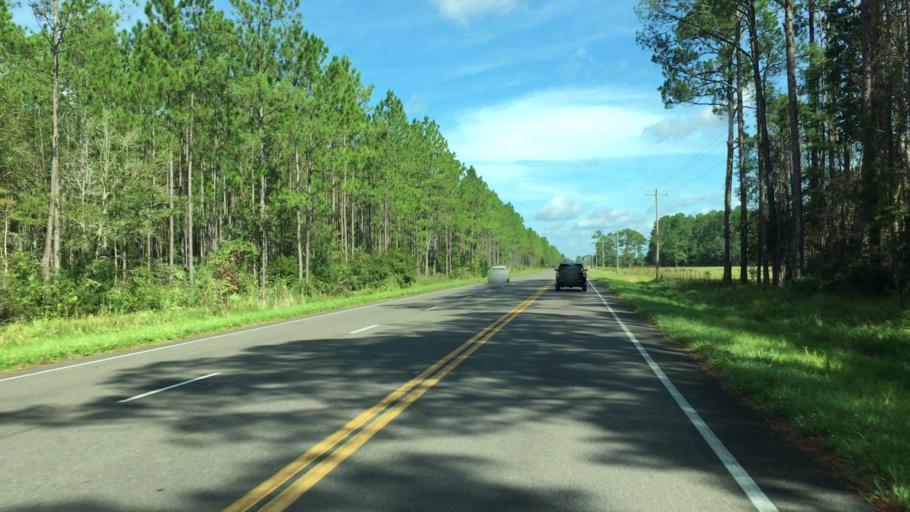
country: US
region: Florida
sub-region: Alachua County
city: Gainesville
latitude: 29.7477
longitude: -82.2774
